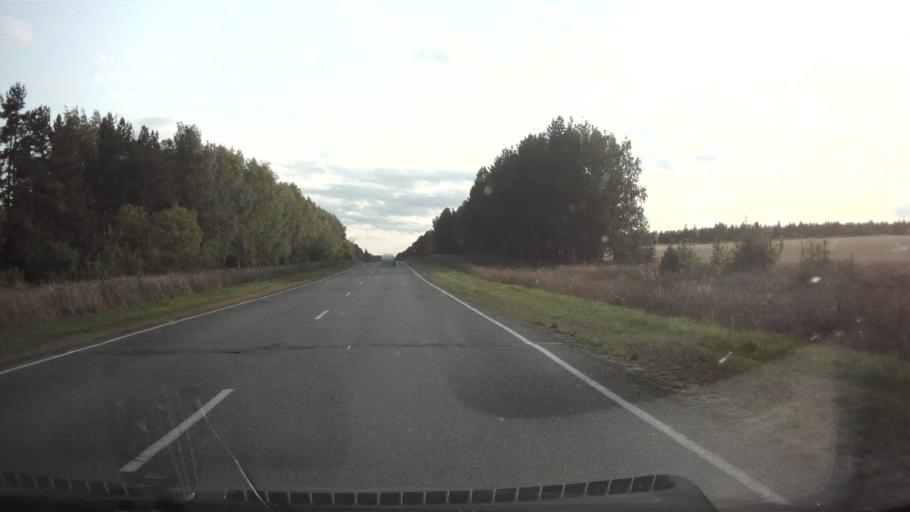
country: RU
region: Mariy-El
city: Kuzhener
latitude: 56.8520
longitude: 48.7491
